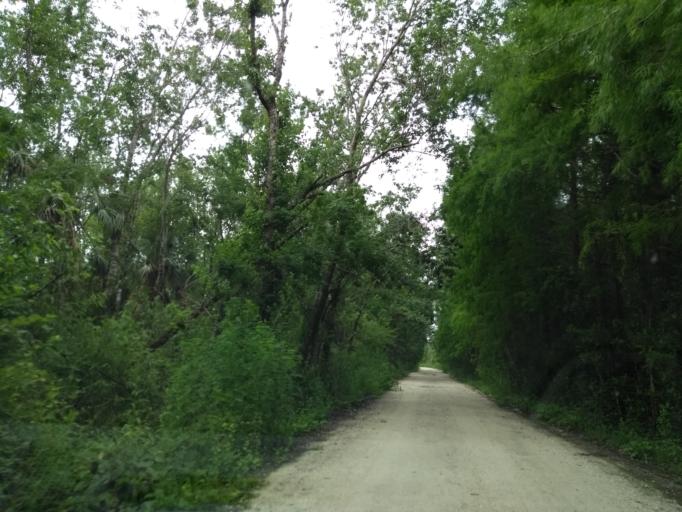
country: US
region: Florida
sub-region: Collier County
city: Lely Resort
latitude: 25.9837
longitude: -81.4109
